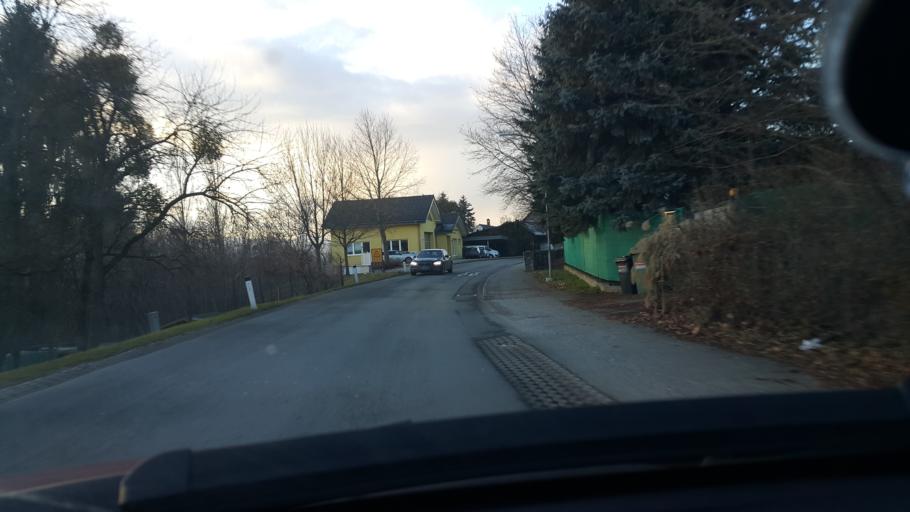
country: AT
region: Styria
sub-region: Politischer Bezirk Graz-Umgebung
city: Lieboch
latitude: 46.9656
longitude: 15.3500
